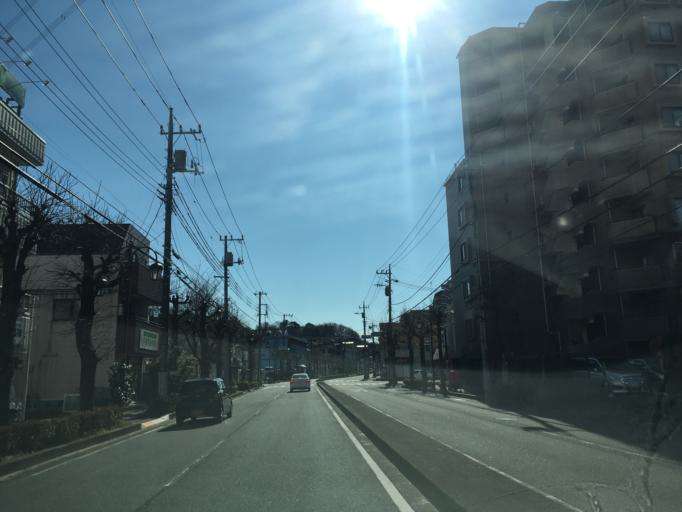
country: JP
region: Tokyo
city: Hino
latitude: 35.6267
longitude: 139.4299
